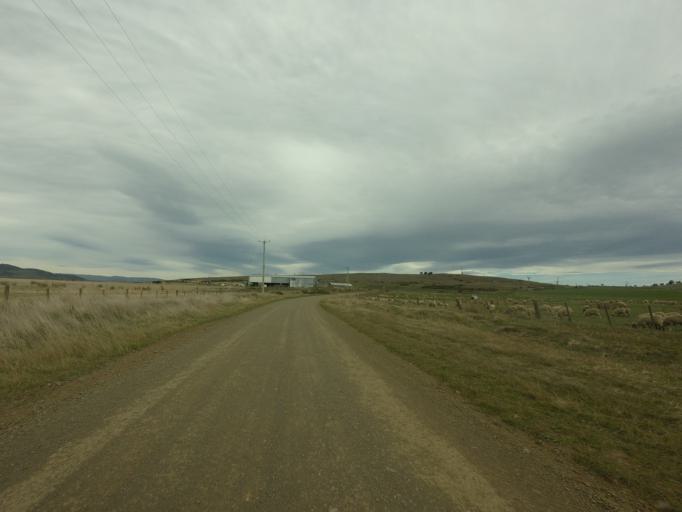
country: AU
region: Tasmania
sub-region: Derwent Valley
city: New Norfolk
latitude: -42.3853
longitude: 146.9852
